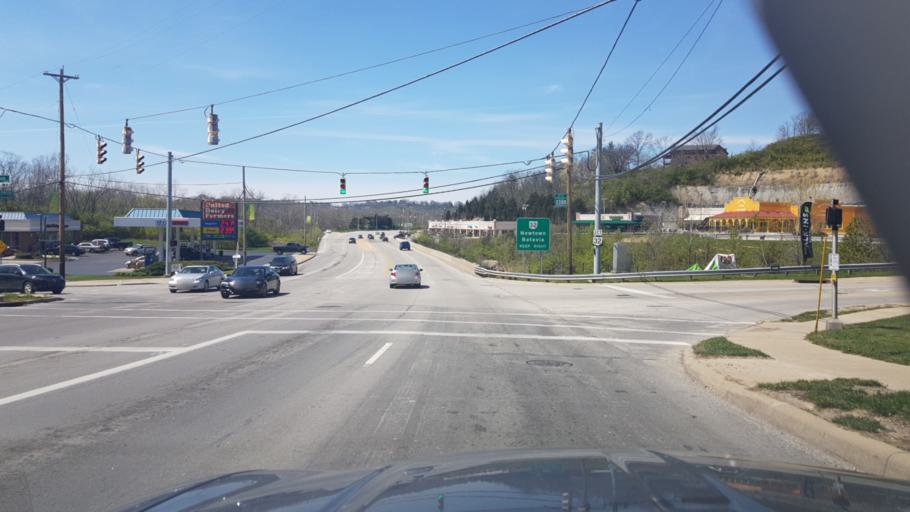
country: US
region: Ohio
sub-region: Hamilton County
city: Turpin Hills
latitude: 39.1055
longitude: -84.3946
